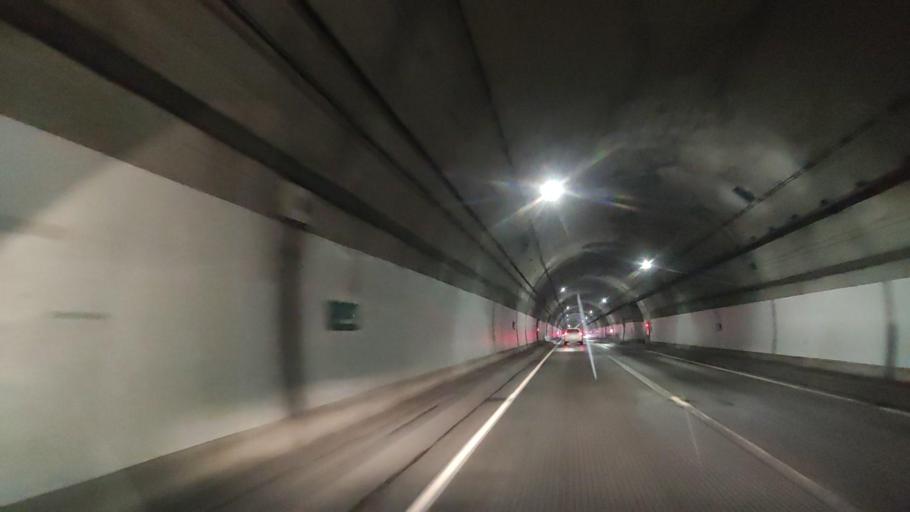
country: JP
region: Hokkaido
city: Rumoi
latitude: 43.7080
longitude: 141.3337
